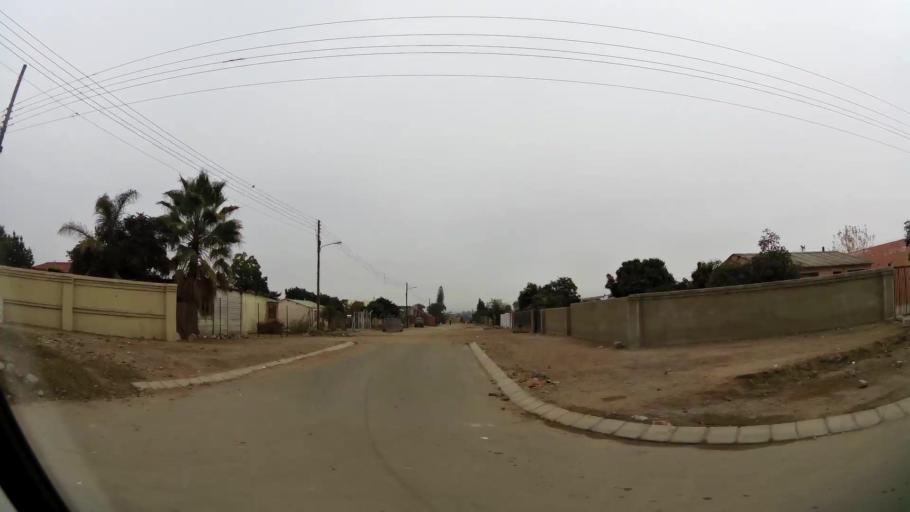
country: ZA
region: Limpopo
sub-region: Capricorn District Municipality
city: Polokwane
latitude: -23.8529
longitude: 29.3954
